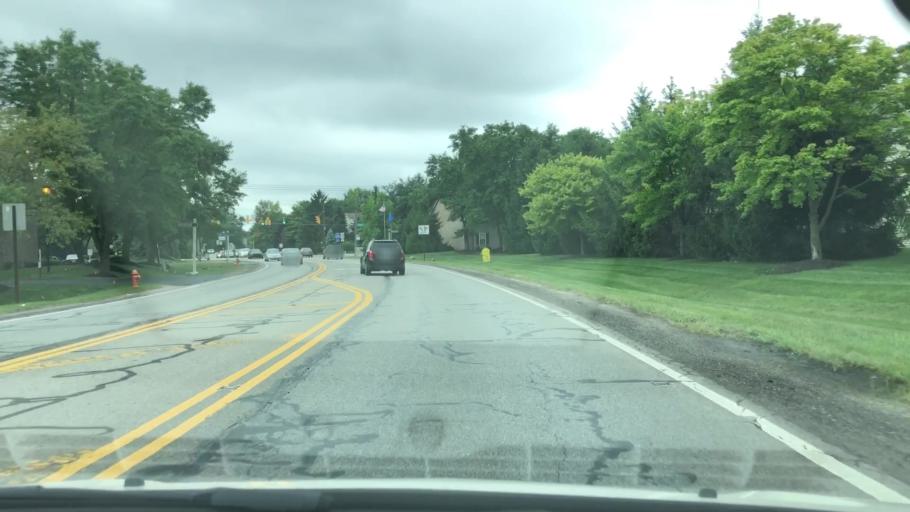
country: US
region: Ohio
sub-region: Franklin County
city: Worthington
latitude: 40.1280
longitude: -82.9937
